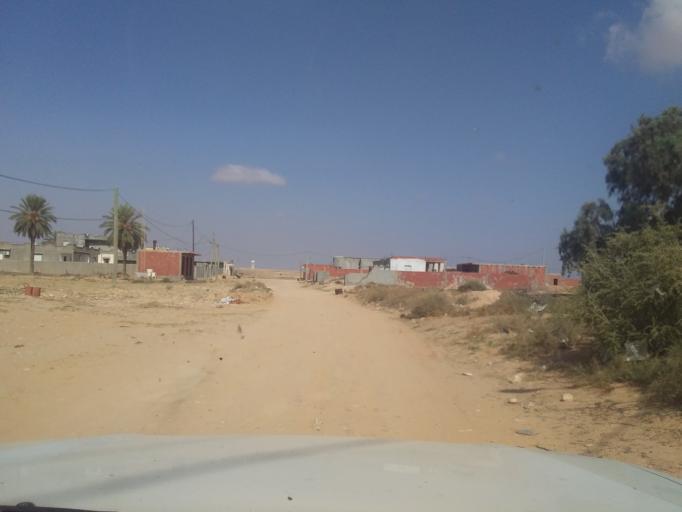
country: TN
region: Qabis
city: Matmata
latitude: 33.6207
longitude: 10.2687
